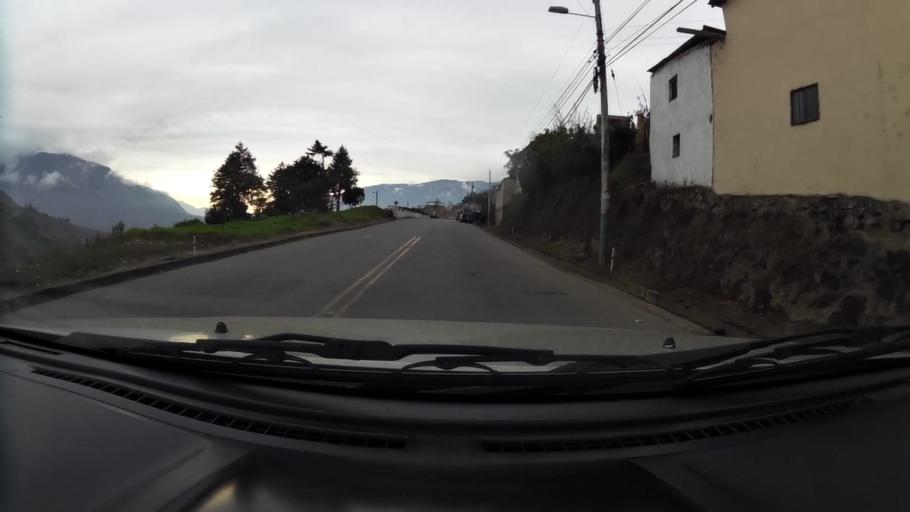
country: EC
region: Chimborazo
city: Alausi
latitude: -2.2916
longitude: -78.9138
